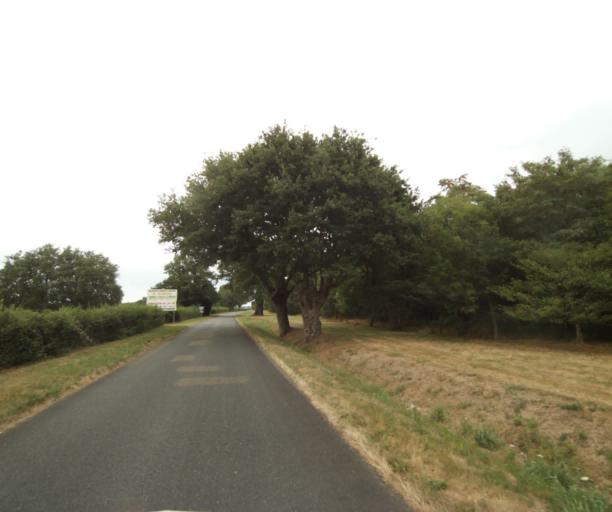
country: FR
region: Pays de la Loire
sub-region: Departement de la Sarthe
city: Sable-sur-Sarthe
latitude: 47.8146
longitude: -0.3508
